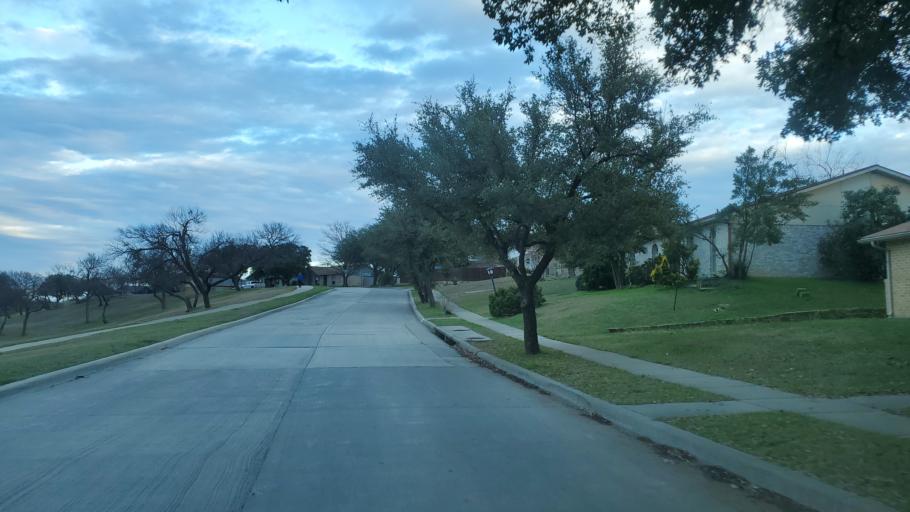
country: US
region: Texas
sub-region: Dallas County
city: Carrollton
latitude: 32.9939
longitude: -96.8859
